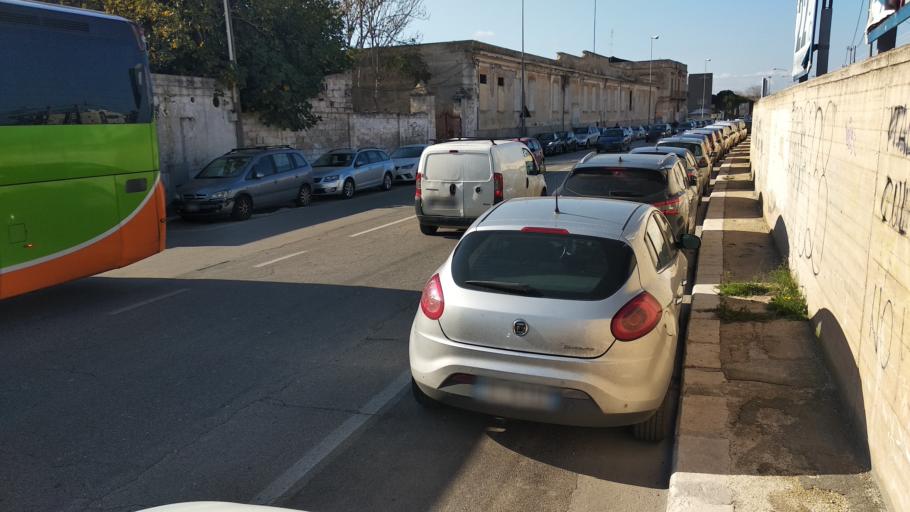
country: IT
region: Apulia
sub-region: Provincia di Bari
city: Bari
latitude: 41.1166
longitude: 16.8553
